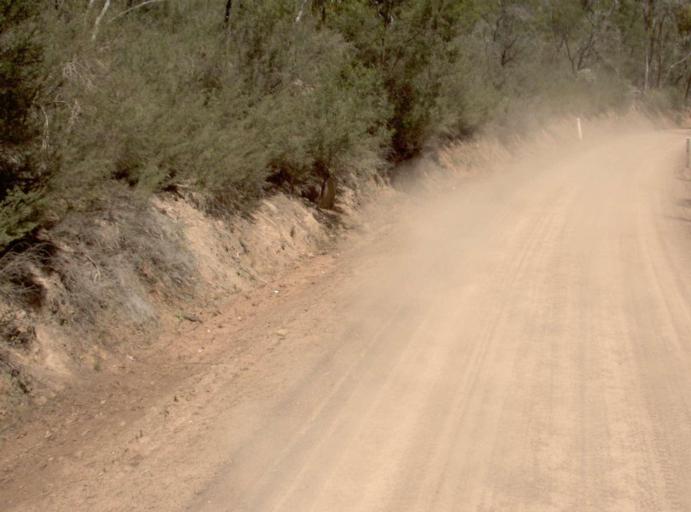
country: AU
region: New South Wales
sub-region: Snowy River
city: Jindabyne
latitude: -37.0392
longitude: 148.5385
